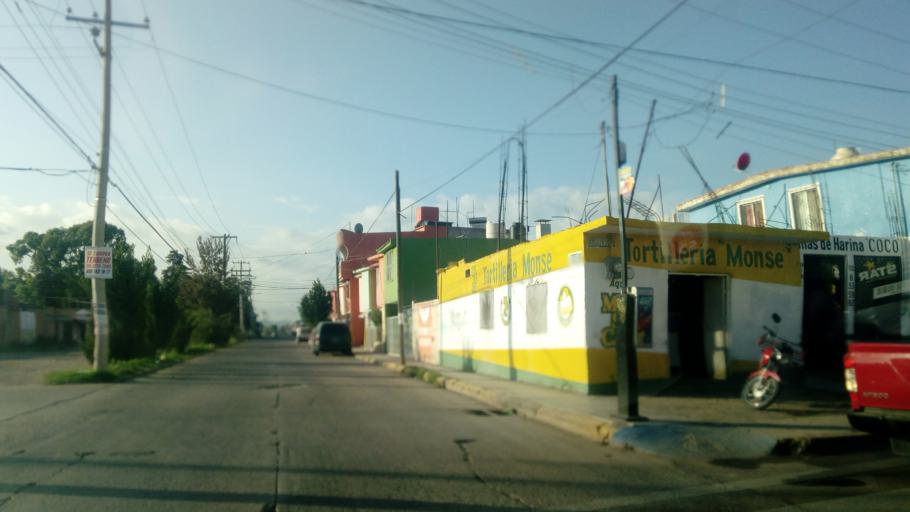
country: MX
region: Durango
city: Victoria de Durango
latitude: 24.0495
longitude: -104.6172
